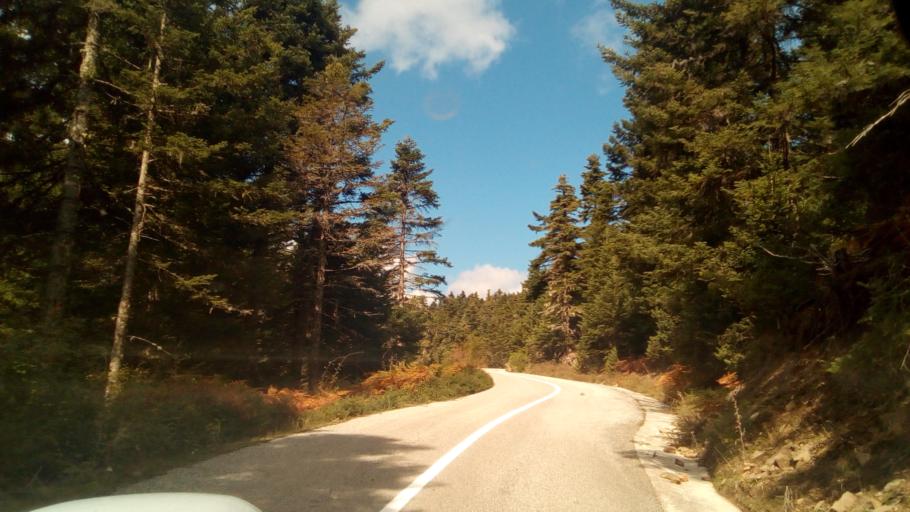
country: GR
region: West Greece
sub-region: Nomos Aitolias kai Akarnanias
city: Nafpaktos
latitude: 38.6396
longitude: 21.9302
